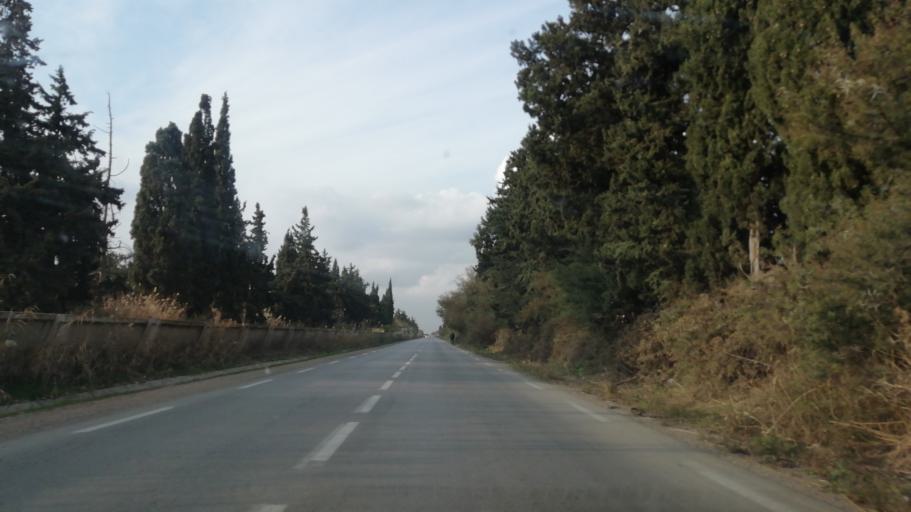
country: DZ
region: Mascara
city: Sig
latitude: 35.6330
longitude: 0.0385
